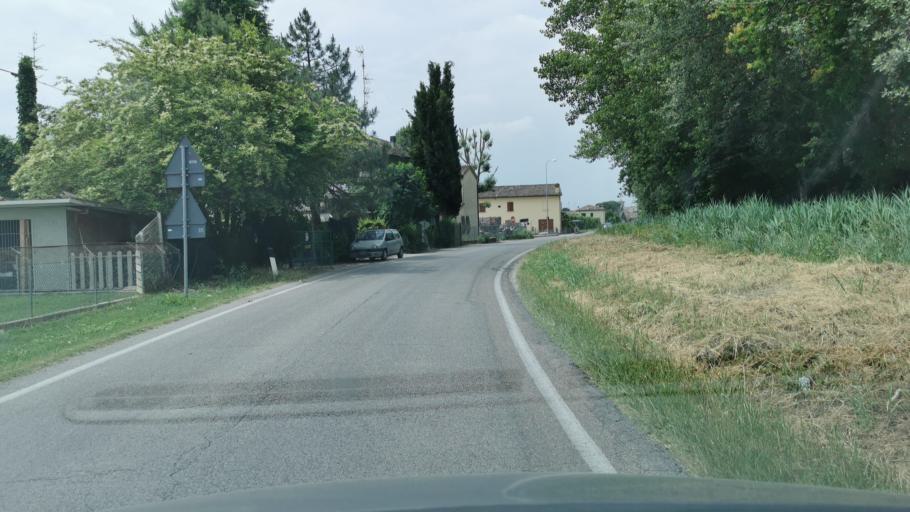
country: IT
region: Emilia-Romagna
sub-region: Provincia di Ravenna
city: Bagnacavallo
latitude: 44.4211
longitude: 11.9873
